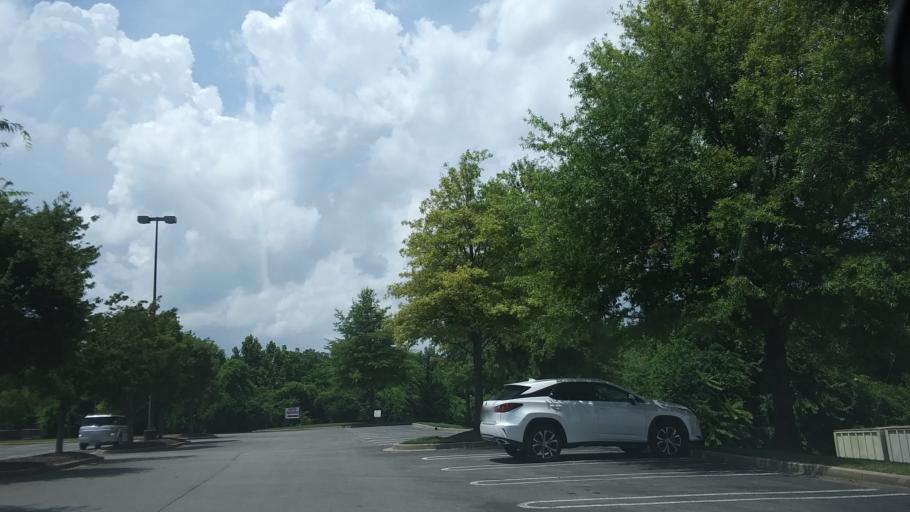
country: US
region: Tennessee
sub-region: Davidson County
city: Belle Meade
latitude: 36.1404
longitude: -86.8846
